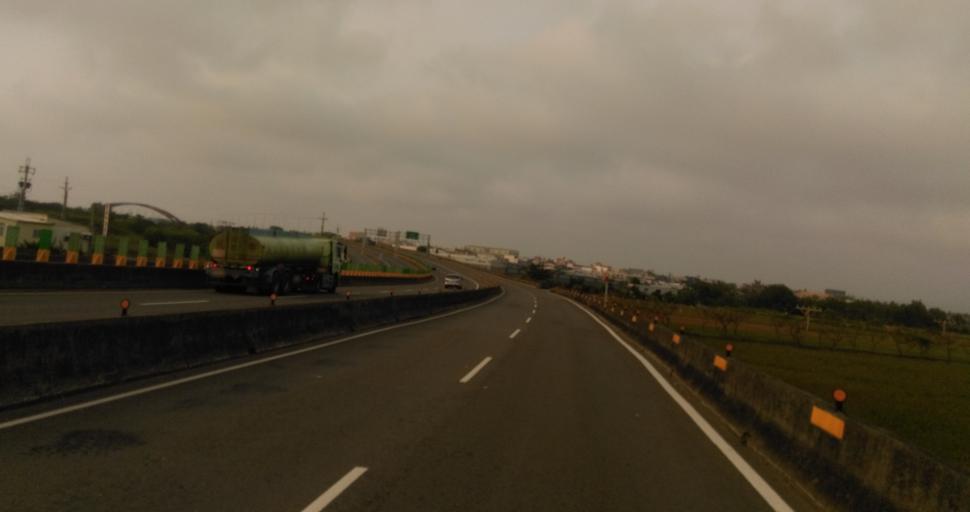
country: TW
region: Taiwan
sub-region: Hsinchu
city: Hsinchu
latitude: 24.8000
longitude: 120.9206
